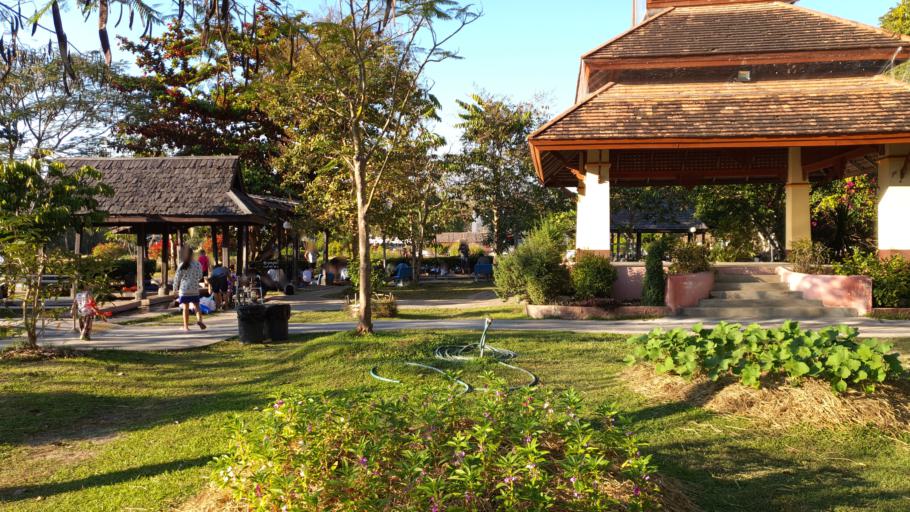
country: TH
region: Chiang Mai
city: Mae On
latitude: 18.8156
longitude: 99.2278
